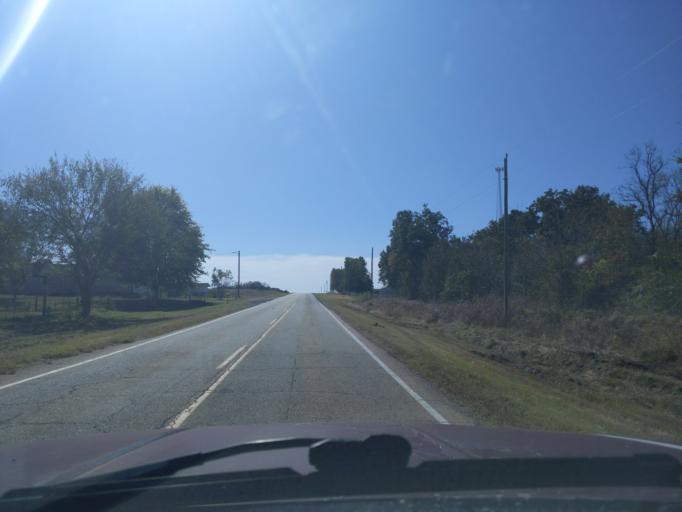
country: US
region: Oklahoma
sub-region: Creek County
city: Bristow
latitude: 35.7238
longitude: -96.3872
